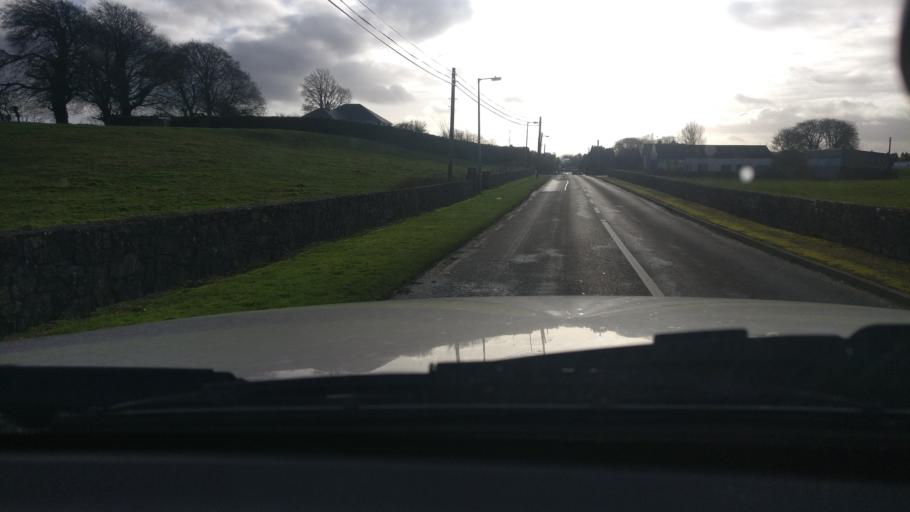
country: IE
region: Connaught
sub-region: County Galway
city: Ballinasloe
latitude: 53.2391
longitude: -8.2711
